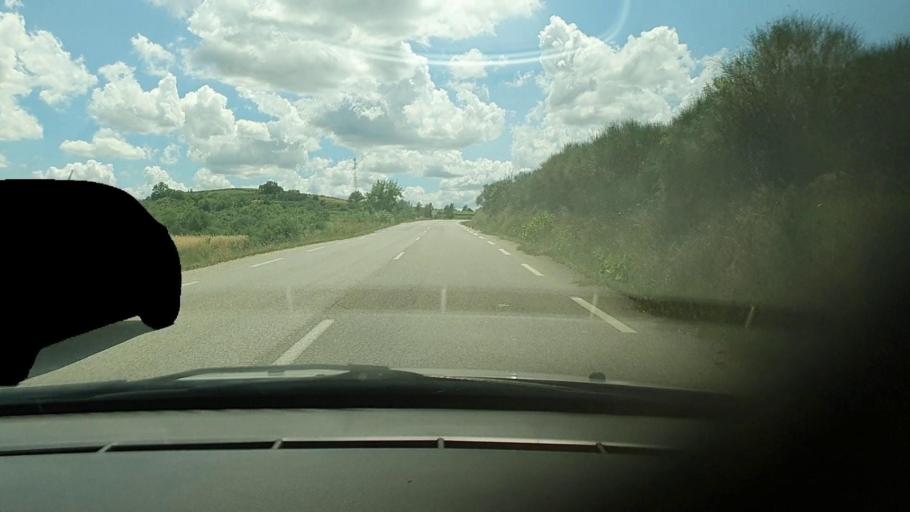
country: FR
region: Languedoc-Roussillon
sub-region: Departement du Gard
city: Mons
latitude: 44.0628
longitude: 4.2233
